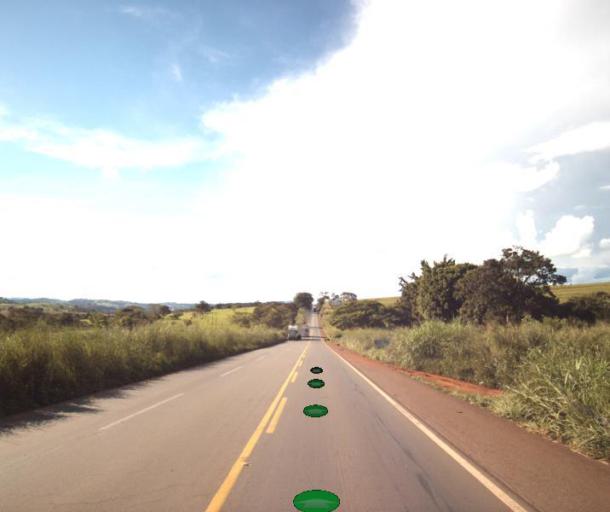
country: BR
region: Goias
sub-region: Rialma
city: Rialma
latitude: -15.3463
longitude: -49.5686
